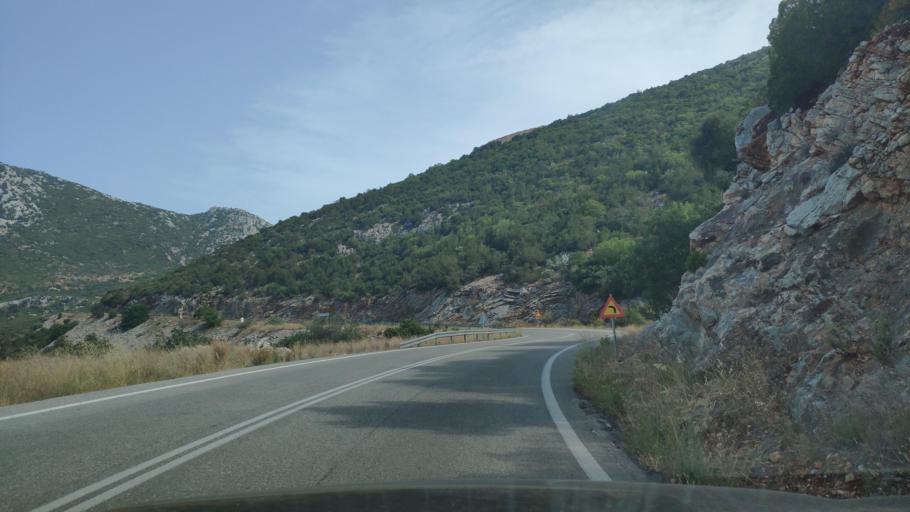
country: GR
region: Peloponnese
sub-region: Nomos Argolidos
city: Palaia Epidavros
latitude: 37.6076
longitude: 23.1554
